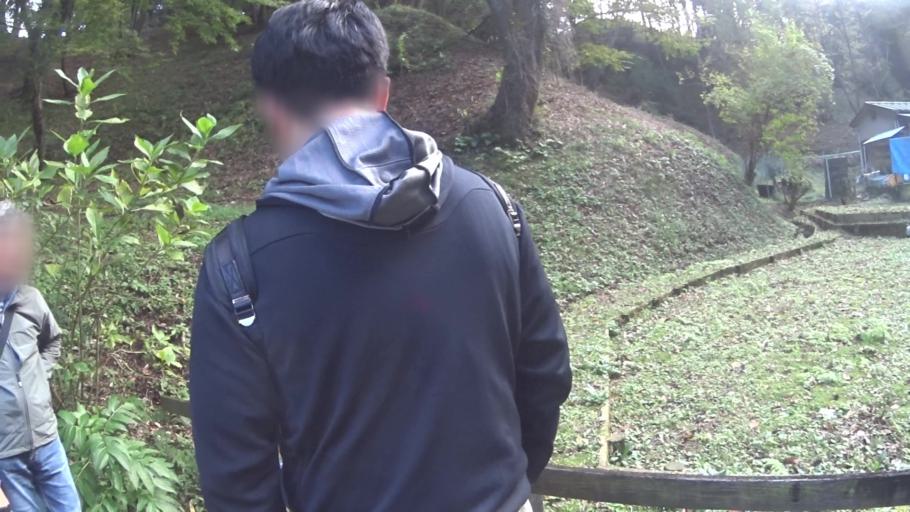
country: JP
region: Tokyo
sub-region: Machida-shi
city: Machida
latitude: 35.5768
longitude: 139.4477
